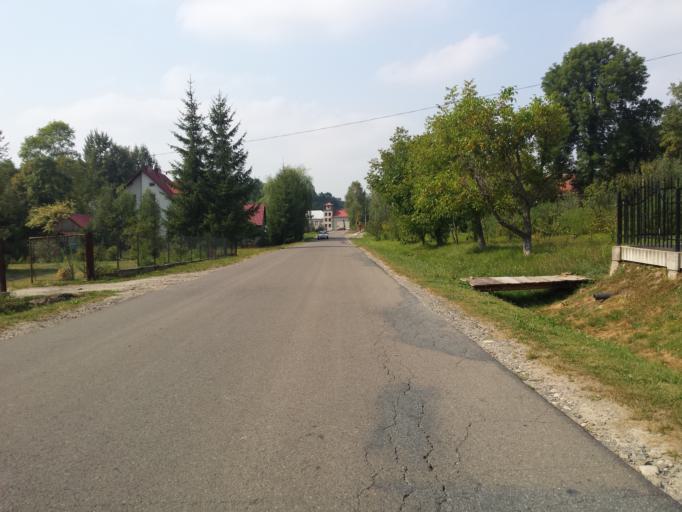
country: PL
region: Subcarpathian Voivodeship
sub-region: Powiat rzeszowski
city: Blazowa
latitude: 49.8532
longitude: 22.1359
